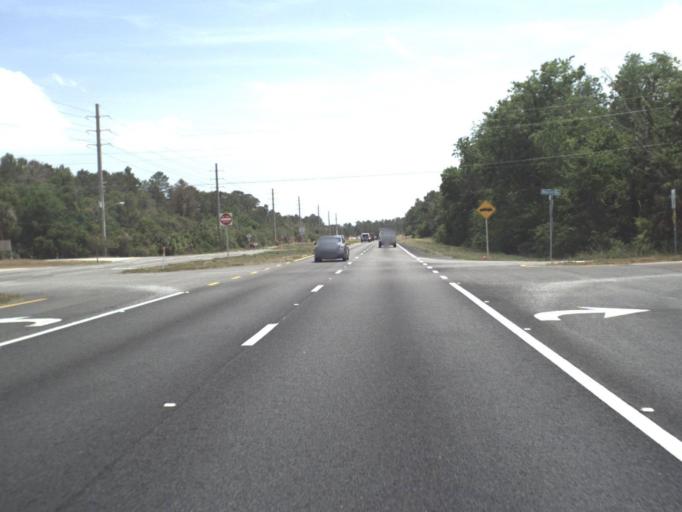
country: US
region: Florida
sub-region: Brevard County
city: Titusville
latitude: 28.5427
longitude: -80.8311
